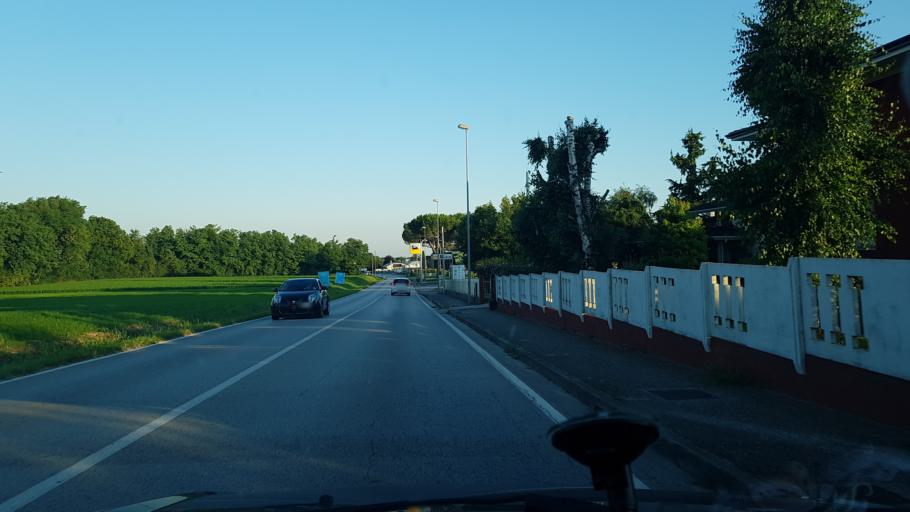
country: IT
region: Friuli Venezia Giulia
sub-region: Provincia di Udine
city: Fagagna
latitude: 46.1061
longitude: 13.0933
